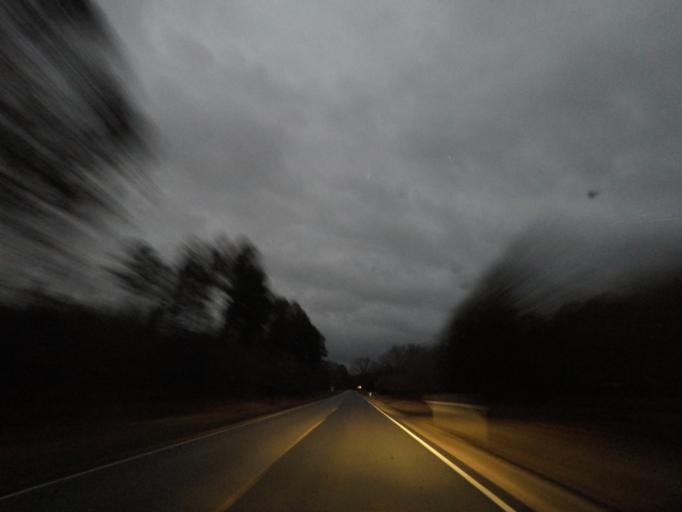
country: US
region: North Carolina
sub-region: Orange County
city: Hillsborough
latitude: 36.0513
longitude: -79.0069
